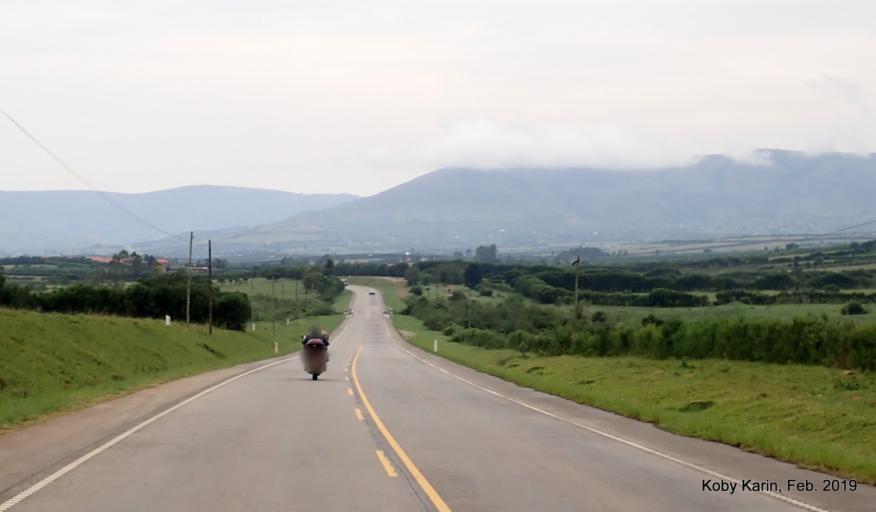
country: UG
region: Western Region
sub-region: Ntungamo District
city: Ntungamo
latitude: -1.0480
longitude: 30.1840
